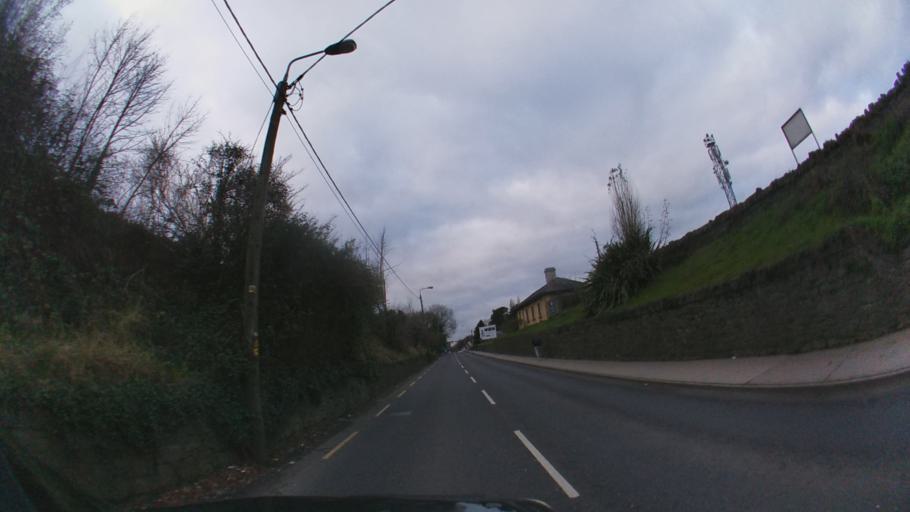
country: IE
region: Leinster
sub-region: Lu
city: Drogheda
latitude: 53.7111
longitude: -6.3358
